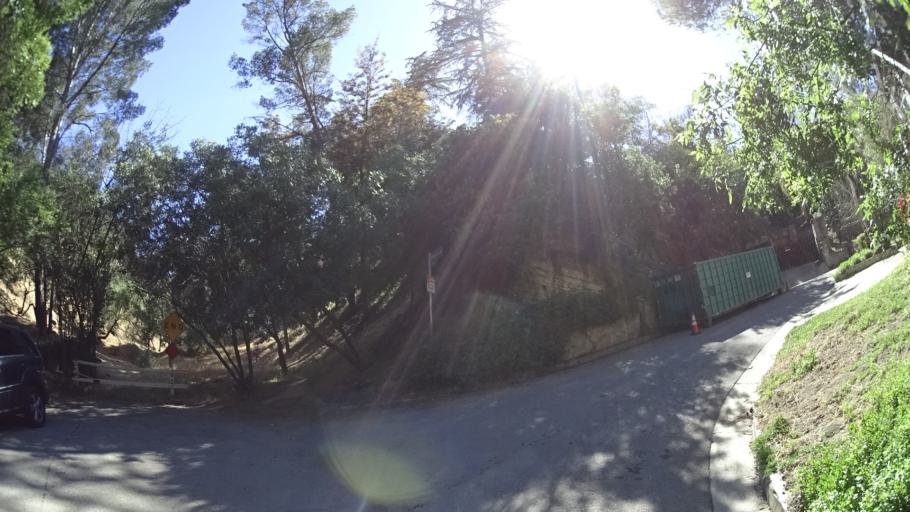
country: US
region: California
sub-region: Los Angeles County
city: Sherman Oaks
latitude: 34.1420
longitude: -118.4539
